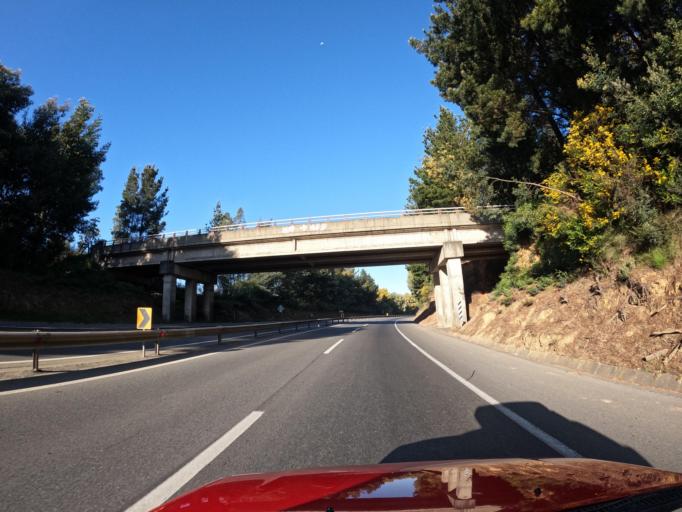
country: CL
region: Biobio
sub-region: Provincia de Concepcion
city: Penco
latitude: -36.7603
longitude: -72.9645
